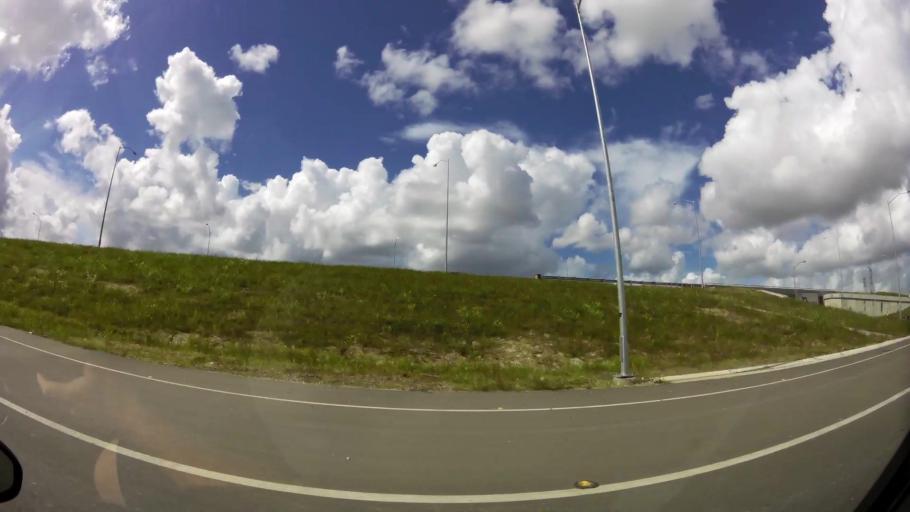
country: TT
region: Penal/Debe
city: Debe
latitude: 10.2162
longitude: -61.4553
